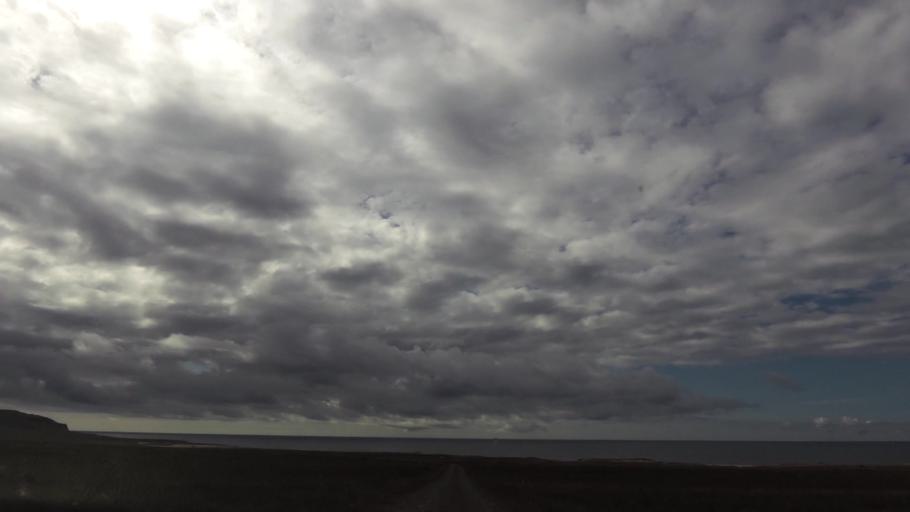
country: IS
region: West
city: Olafsvik
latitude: 65.6142
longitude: -24.3177
